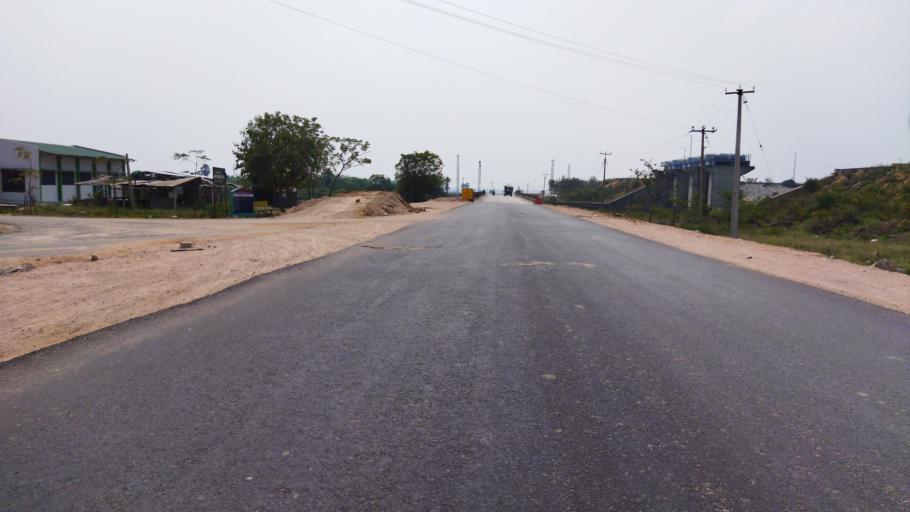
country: IN
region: Telangana
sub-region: Nalgonda
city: Nalgonda
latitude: 17.0753
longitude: 79.3187
